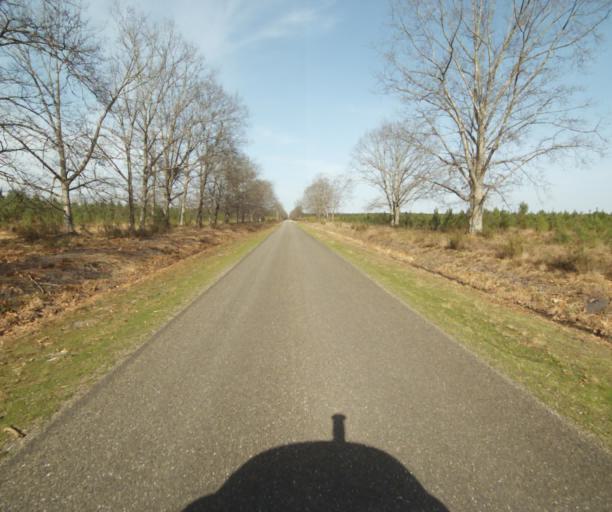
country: FR
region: Aquitaine
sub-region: Departement des Landes
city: Roquefort
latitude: 44.1633
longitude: -0.1660
